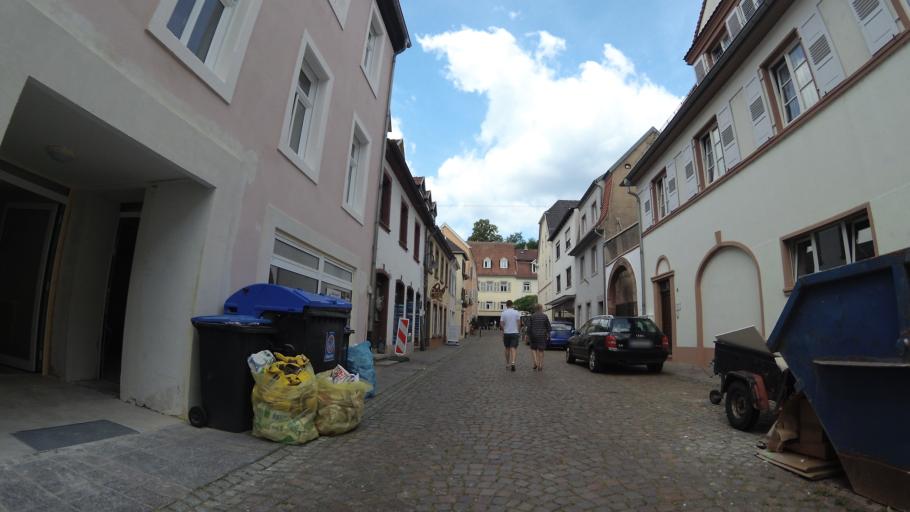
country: DE
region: Saarland
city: Blieskastel
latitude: 49.2380
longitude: 7.2592
